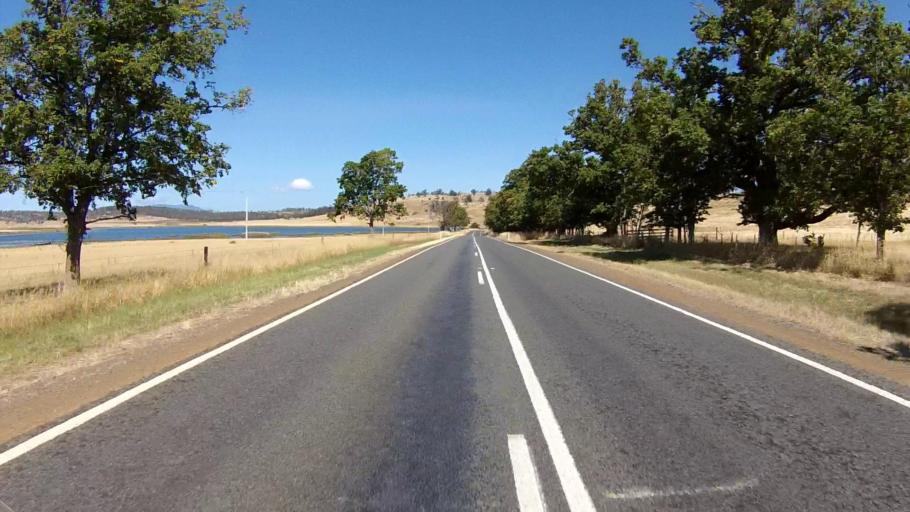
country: AU
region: Tasmania
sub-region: Sorell
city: Sorell
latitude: -42.4841
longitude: 147.9338
